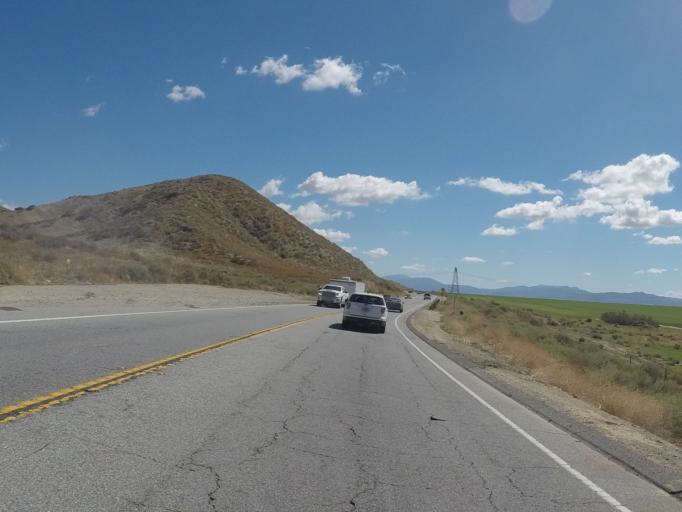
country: US
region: California
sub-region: Riverside County
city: Lakeview
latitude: 33.8689
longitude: -117.0422
